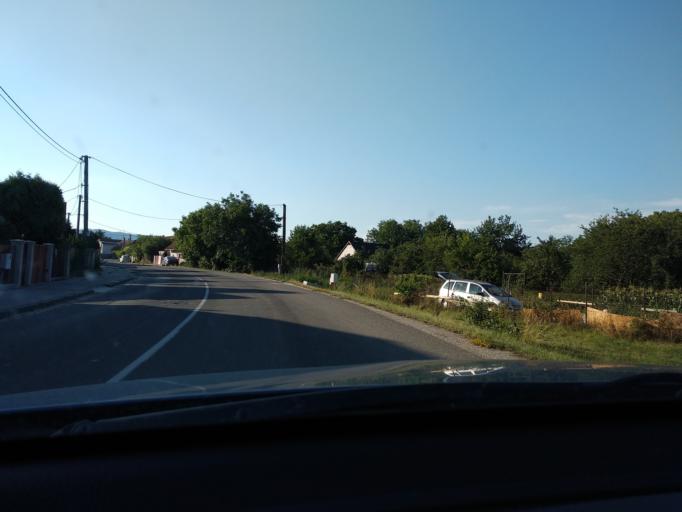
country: SK
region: Trenciansky
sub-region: Okres Trencin
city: Trencin
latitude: 48.8752
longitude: 18.0225
